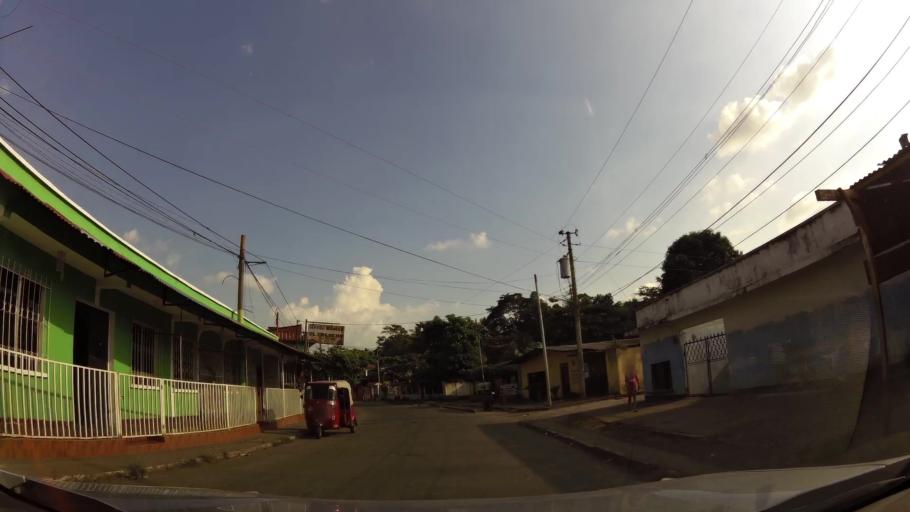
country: GT
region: Retalhuleu
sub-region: Municipio de Retalhuleu
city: Retalhuleu
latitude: 14.5296
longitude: -91.6753
